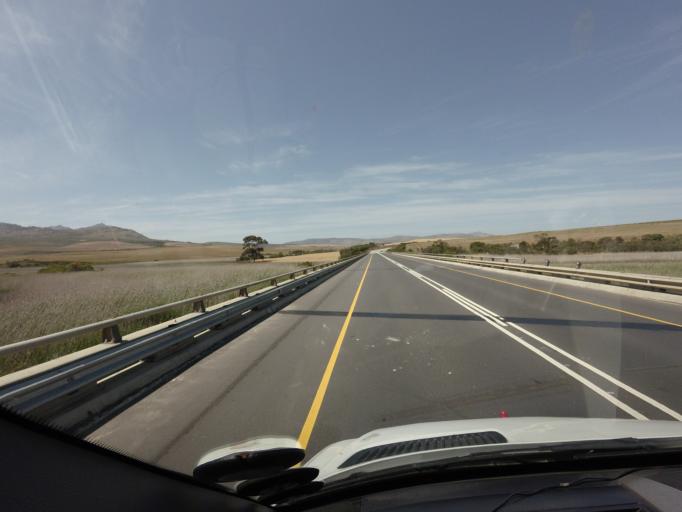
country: ZA
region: Western Cape
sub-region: Overberg District Municipality
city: Hermanus
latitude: -34.3115
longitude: 19.1476
